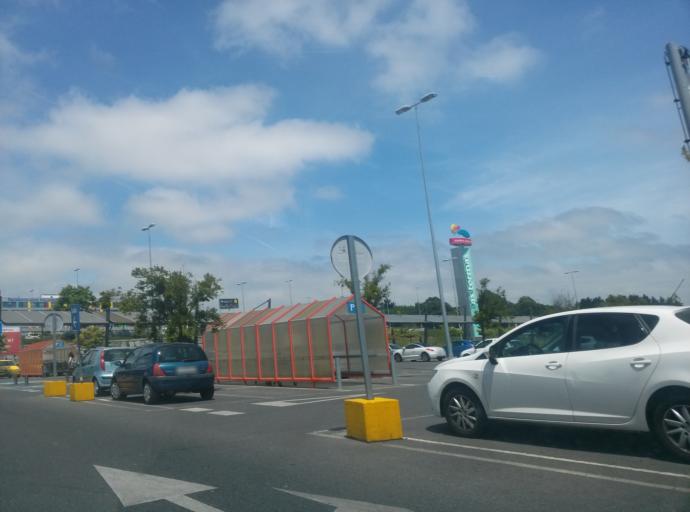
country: ES
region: Galicia
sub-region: Provincia de Lugo
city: Lugo
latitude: 43.0369
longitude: -7.5675
